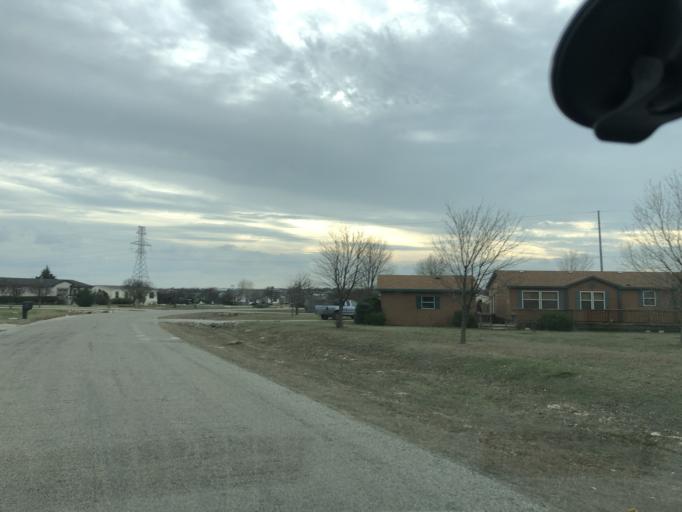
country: US
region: Texas
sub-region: Tarrant County
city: Saginaw
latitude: 32.9034
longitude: -97.3804
